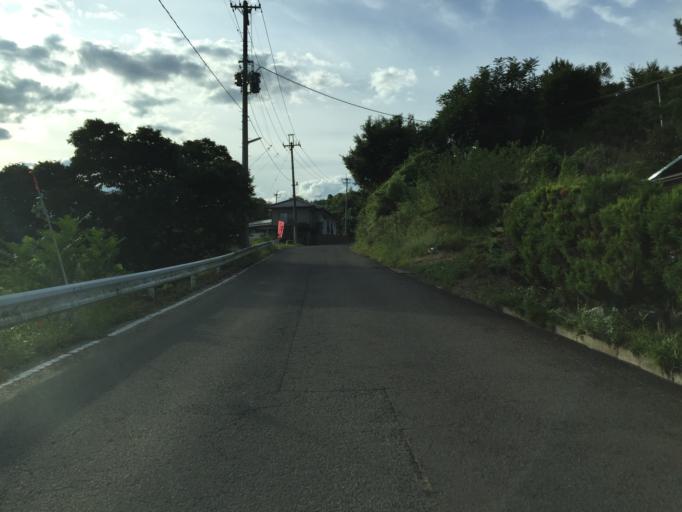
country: JP
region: Fukushima
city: Hobaramachi
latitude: 37.7971
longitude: 140.5308
